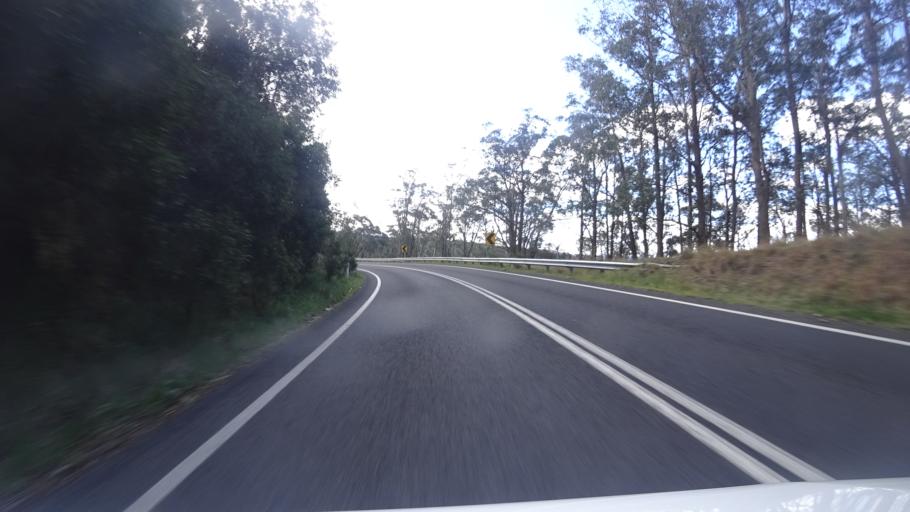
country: AU
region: New South Wales
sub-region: Lithgow
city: Bowenfels
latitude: -33.6698
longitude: 150.0519
